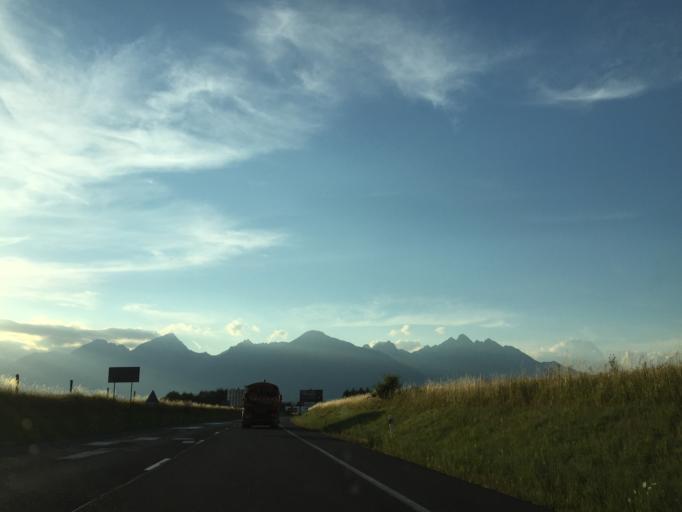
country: SK
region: Presovsky
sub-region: Okres Poprad
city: Poprad
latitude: 49.0762
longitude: 20.2728
